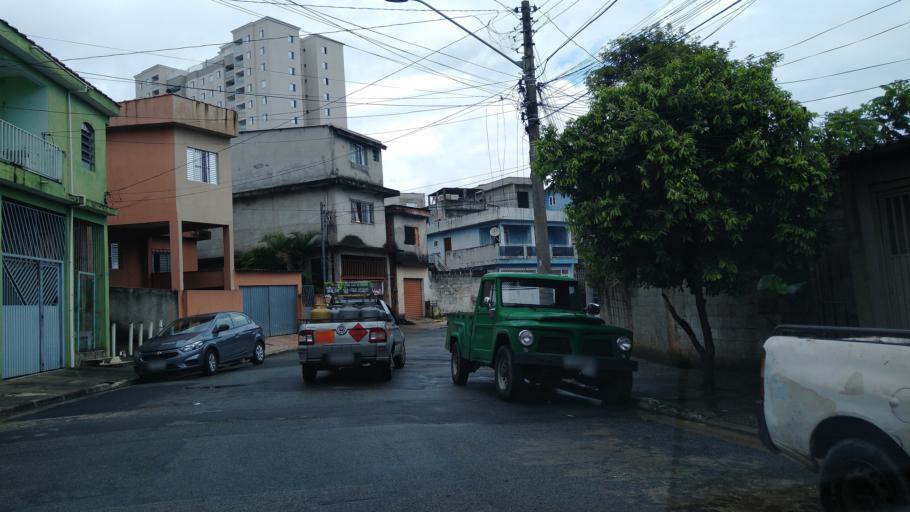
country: BR
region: Sao Paulo
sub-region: Aruja
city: Aruja
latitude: -23.4160
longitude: -46.4061
